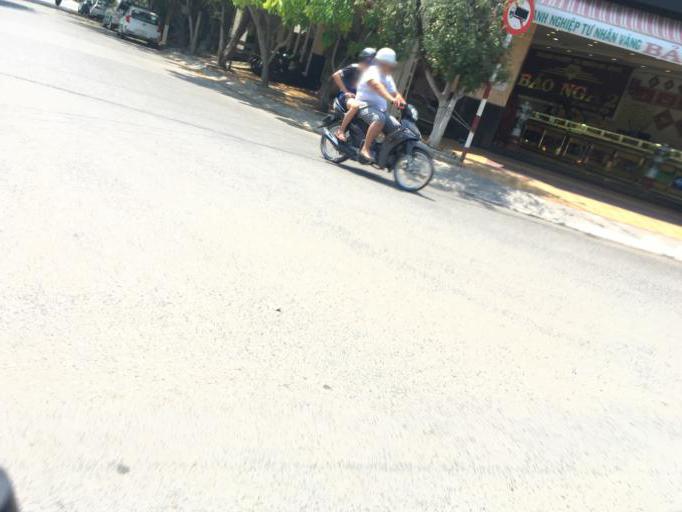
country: VN
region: Ninh Thuan
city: Phan Rang-Thap Cham
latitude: 11.5684
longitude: 108.9949
